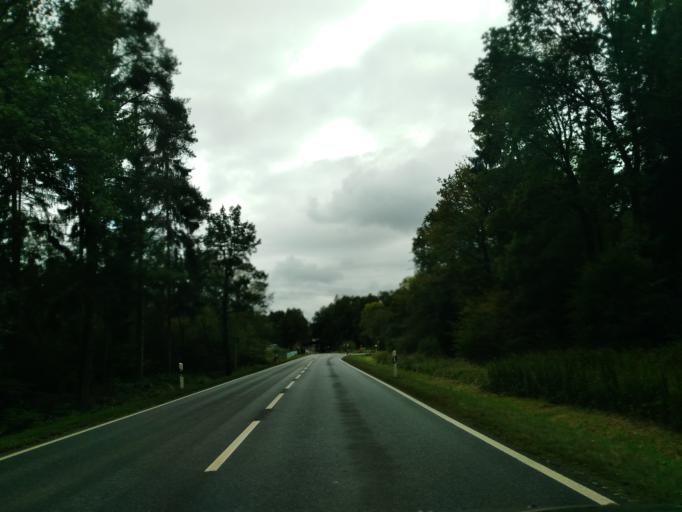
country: DE
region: Rheinland-Pfalz
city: Vettelschoss
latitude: 50.6209
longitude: 7.3083
